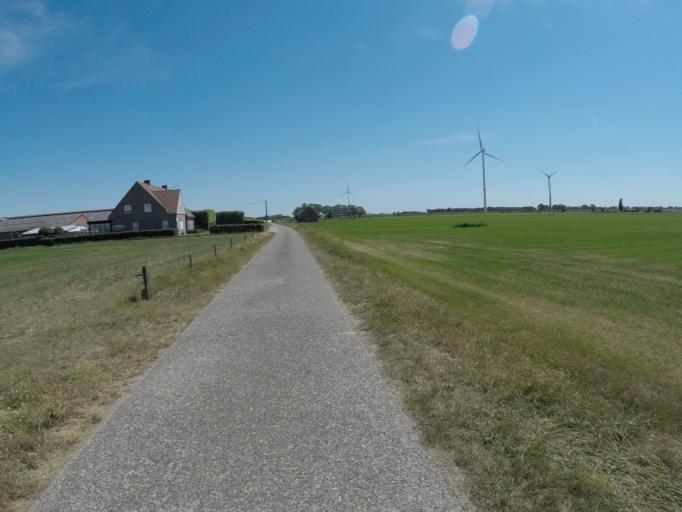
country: NL
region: North Brabant
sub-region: Gemeente Zundert
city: Zundert
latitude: 51.4113
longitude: 4.6861
